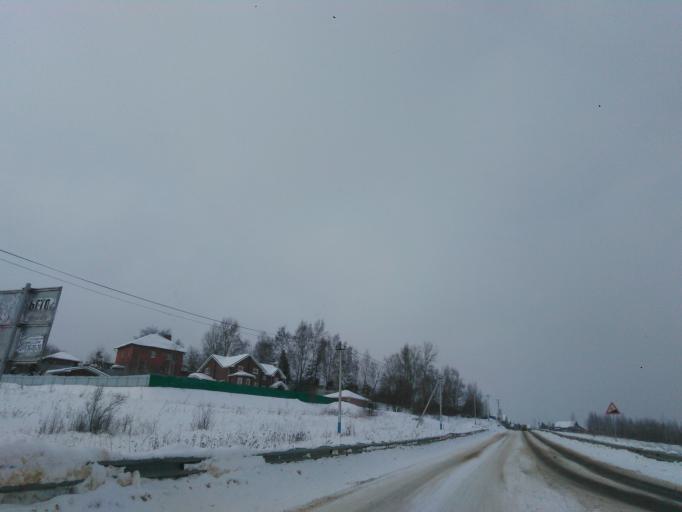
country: RU
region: Moskovskaya
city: Yakhroma
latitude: 56.2710
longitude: 37.4894
